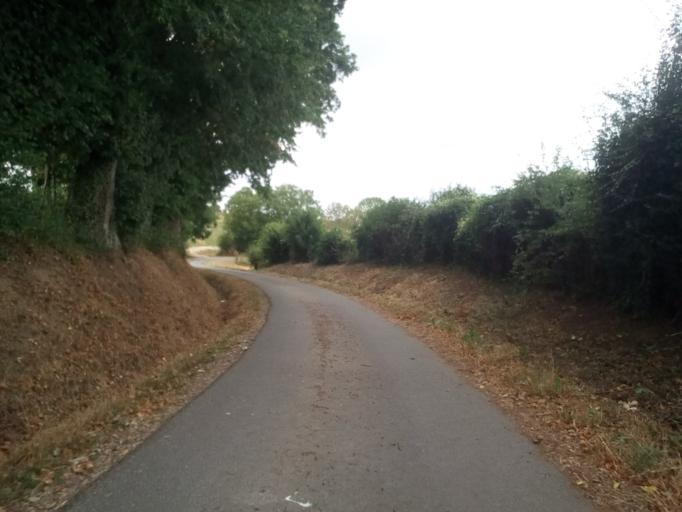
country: FR
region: Lower Normandy
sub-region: Departement du Calvados
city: Troarn
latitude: 49.1642
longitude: -0.1618
